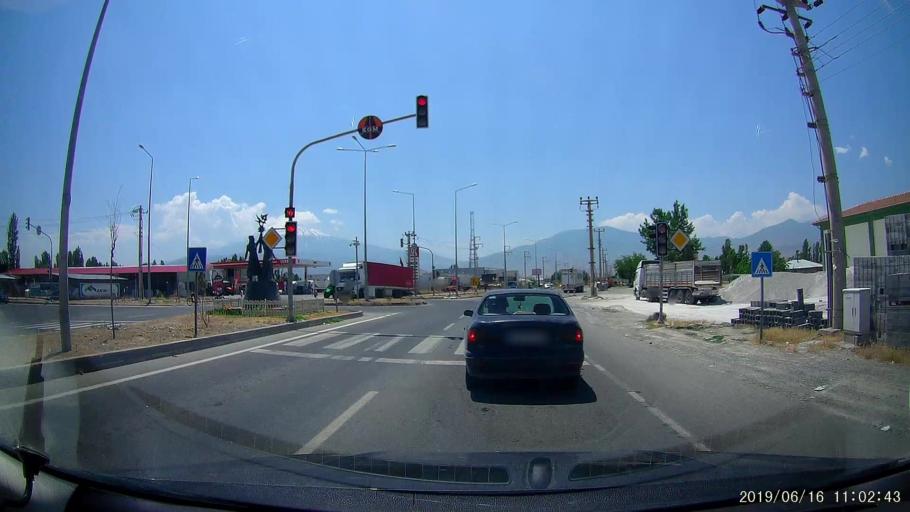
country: TR
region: Igdir
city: Igdir
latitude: 39.9045
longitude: 44.0607
